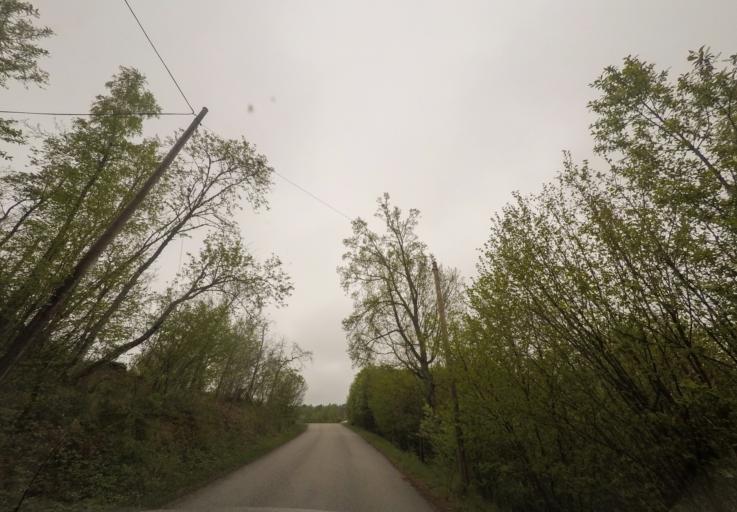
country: SE
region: Vaestmanland
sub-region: Vasteras
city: Vasteras
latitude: 59.5673
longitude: 16.6227
